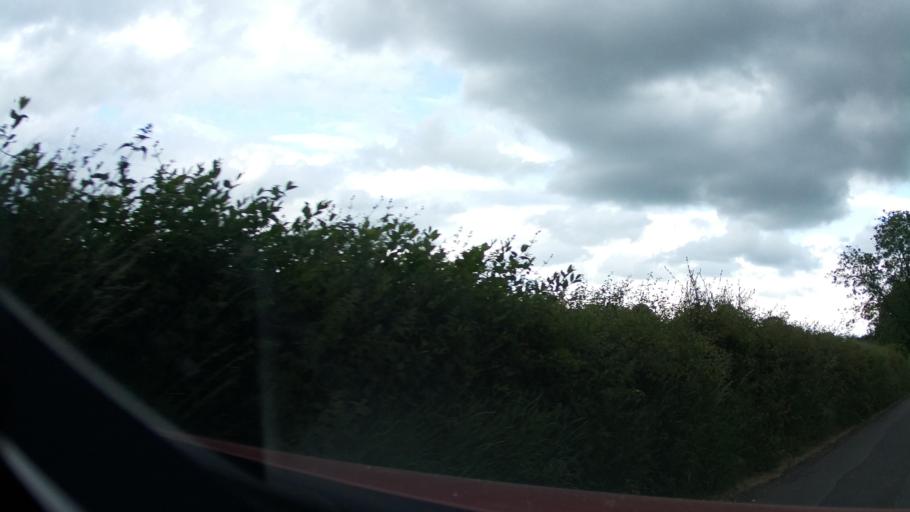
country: GB
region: England
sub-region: South Gloucestershire
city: Siston
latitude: 51.4599
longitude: -2.4470
